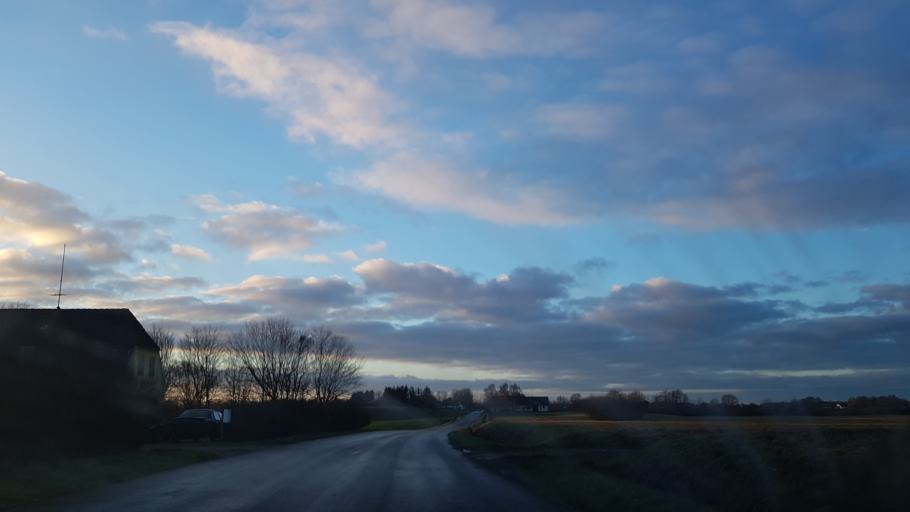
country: DK
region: South Denmark
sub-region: Kolding Kommune
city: Vamdrup
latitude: 55.3745
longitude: 9.2876
